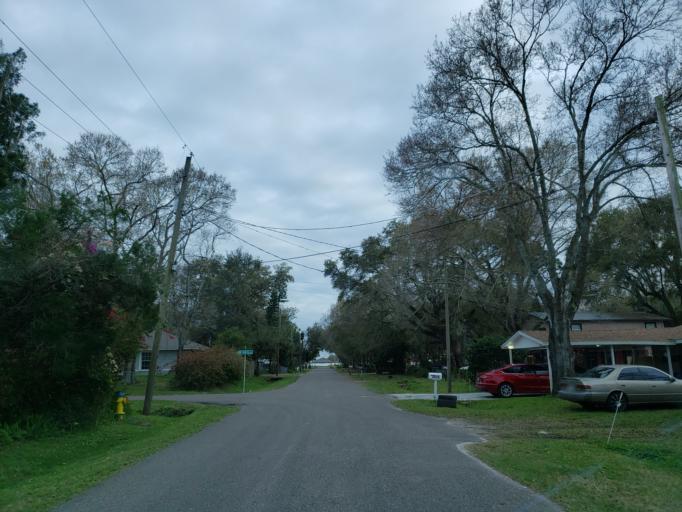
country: US
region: Florida
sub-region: Hillsborough County
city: Palm River-Clair Mel
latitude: 27.9180
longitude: -82.3728
